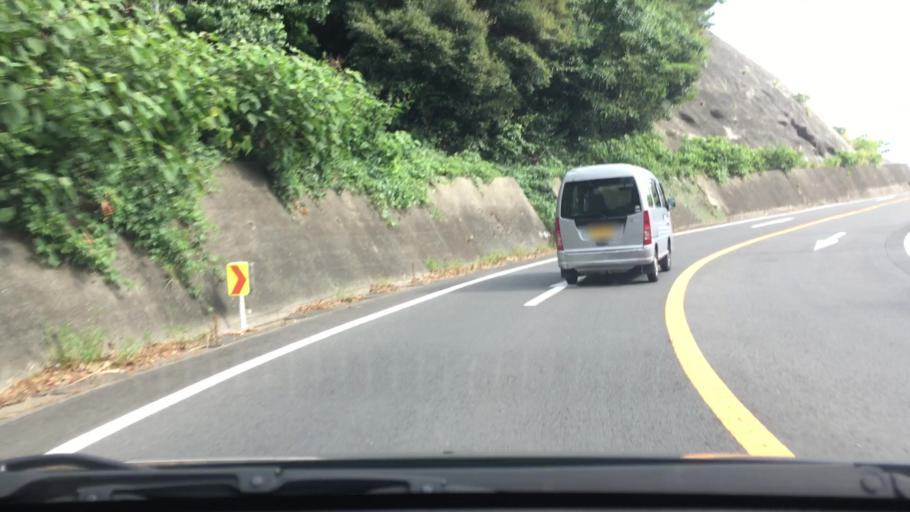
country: JP
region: Nagasaki
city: Togitsu
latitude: 32.8375
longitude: 129.7052
